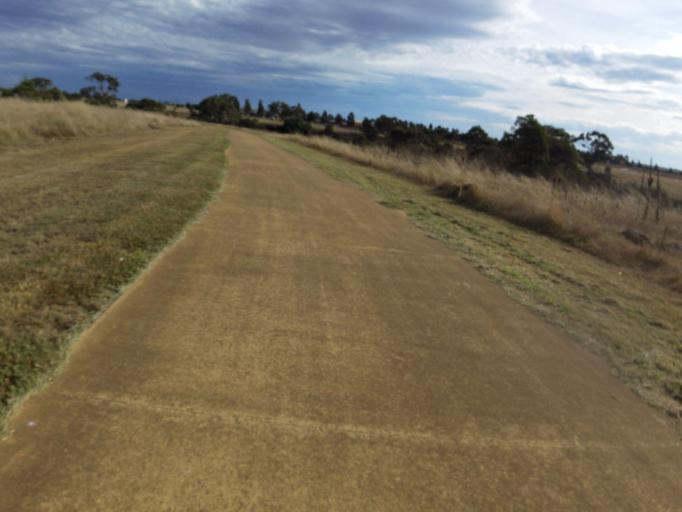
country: AU
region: Victoria
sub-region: Melton
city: Melton South
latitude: -37.7295
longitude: 144.5797
